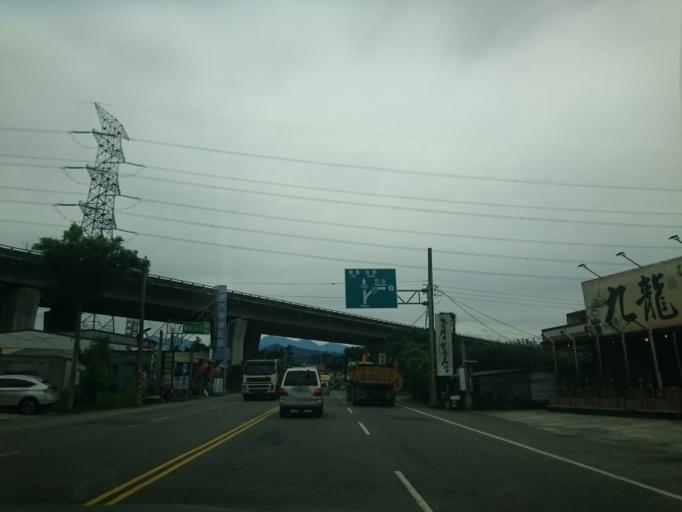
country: TW
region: Taiwan
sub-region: Nantou
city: Nantou
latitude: 23.8343
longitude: 120.7070
